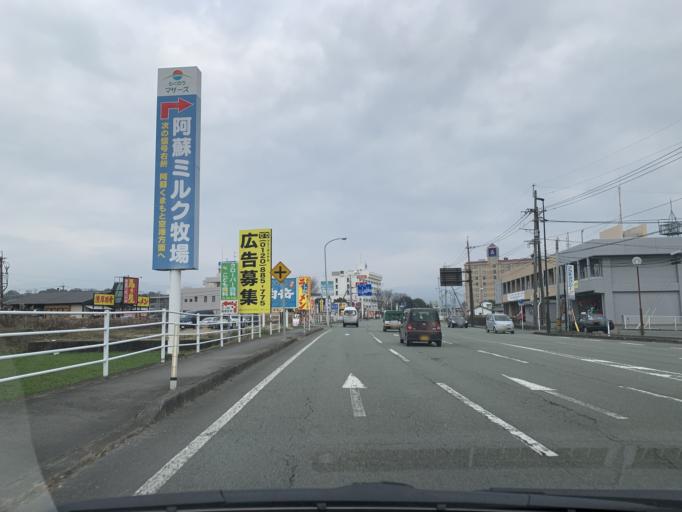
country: JP
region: Kumamoto
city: Ozu
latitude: 32.8750
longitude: 130.8501
